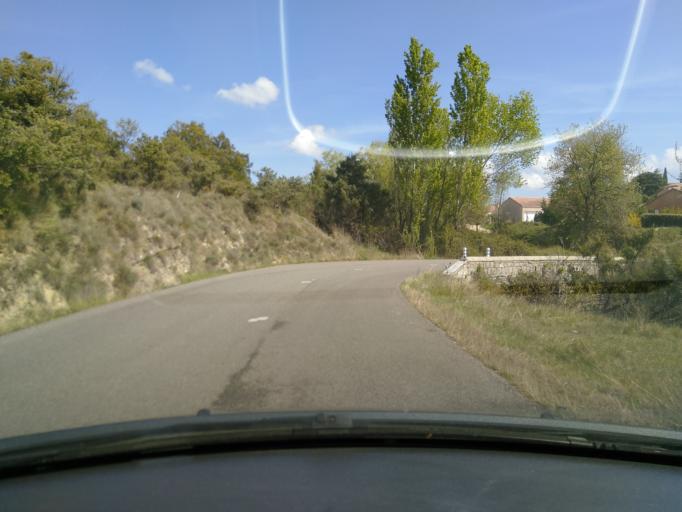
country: FR
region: Rhone-Alpes
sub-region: Departement de l'Ardeche
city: Ruoms
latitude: 44.4535
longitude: 4.3951
